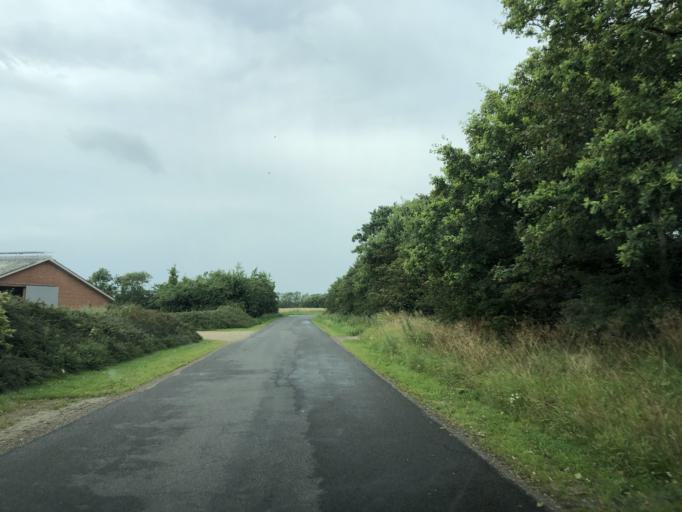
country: DK
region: Central Jutland
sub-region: Ringkobing-Skjern Kommune
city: Skjern
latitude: 55.8951
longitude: 8.4415
